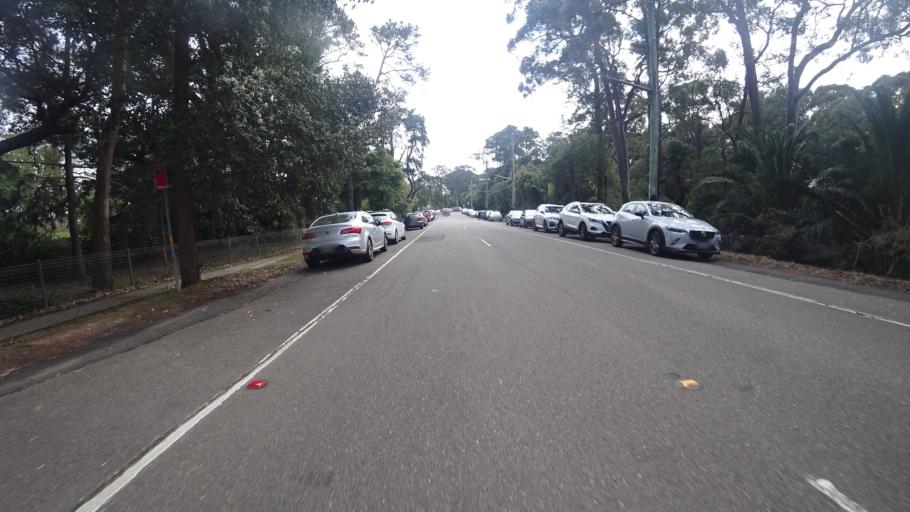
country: AU
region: New South Wales
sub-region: City of Sydney
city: North Turramurra
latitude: -33.6902
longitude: 151.1520
